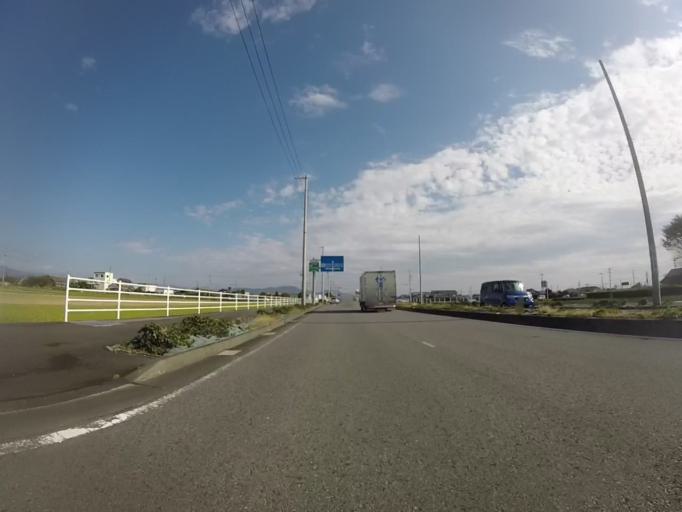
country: JP
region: Shizuoka
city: Fujieda
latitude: 34.8192
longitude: 138.2588
